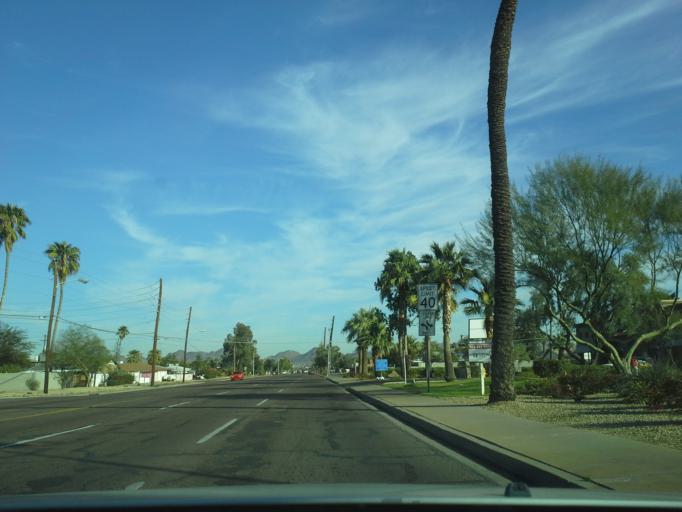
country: US
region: Arizona
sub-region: Maricopa County
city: Glendale
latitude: 33.5676
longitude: -112.0987
